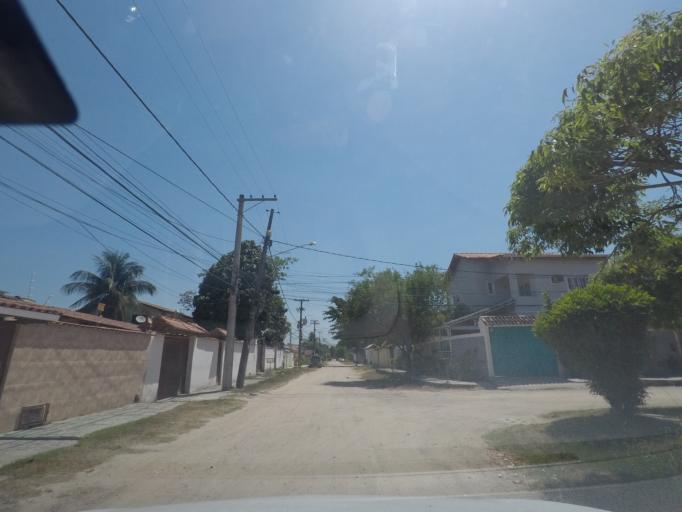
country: BR
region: Rio de Janeiro
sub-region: Niteroi
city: Niteroi
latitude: -22.9351
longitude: -43.0161
